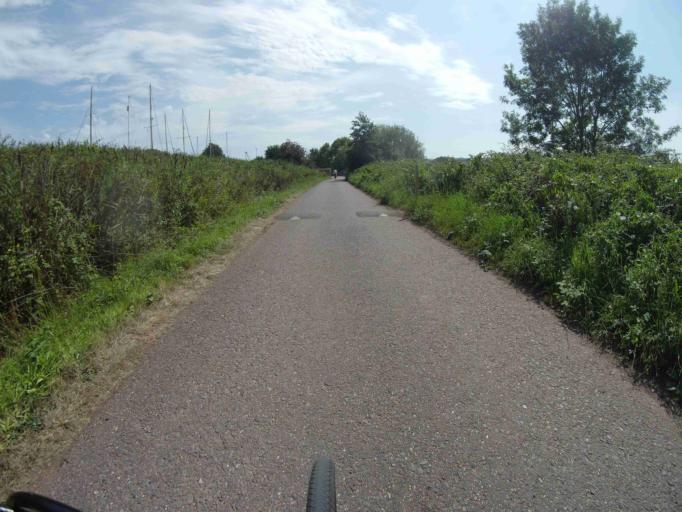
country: GB
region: England
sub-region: Devon
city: Topsham
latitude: 50.6657
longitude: -3.4684
